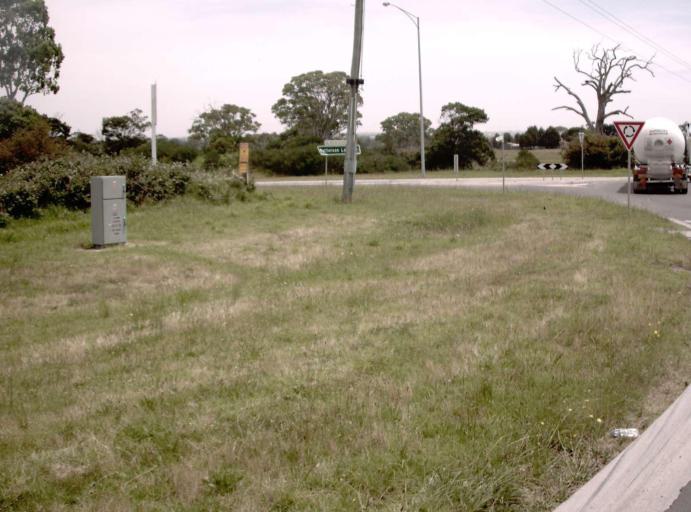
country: AU
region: Victoria
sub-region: Casey
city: Lynbrook
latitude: -38.0633
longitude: 145.2421
